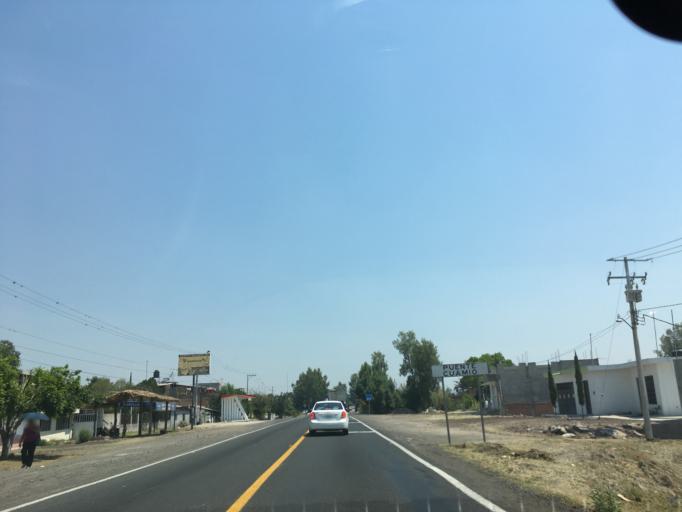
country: MX
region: Michoacan
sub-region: Cuitzeo
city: Cuamio
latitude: 20.0321
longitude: -101.1527
